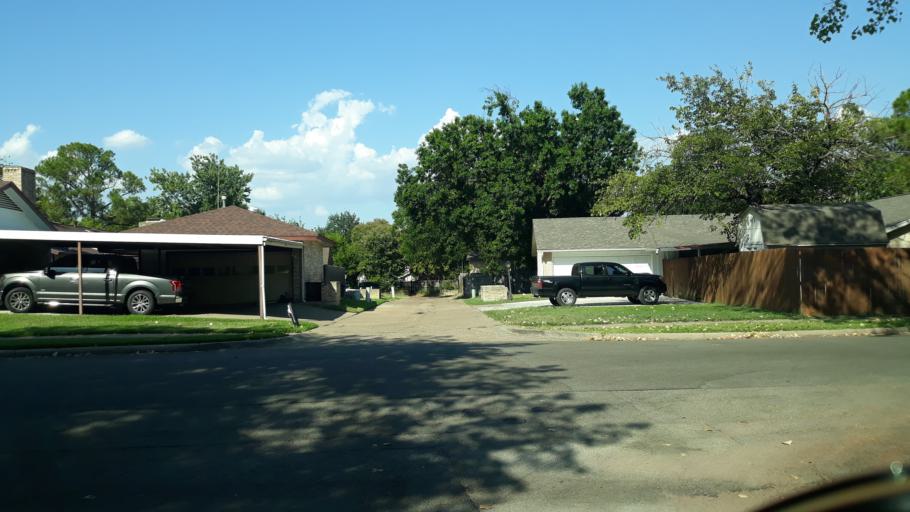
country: US
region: Texas
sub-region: Dallas County
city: Irving
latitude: 32.8475
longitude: -97.0052
